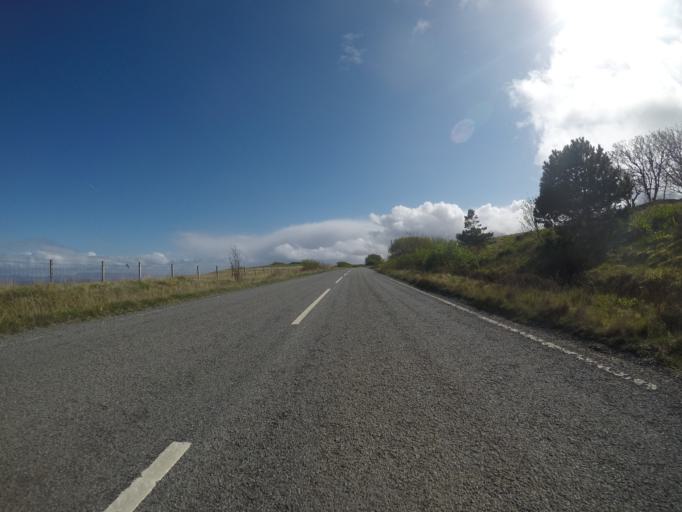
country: GB
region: Scotland
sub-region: Highland
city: Portree
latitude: 57.5904
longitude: -6.1584
